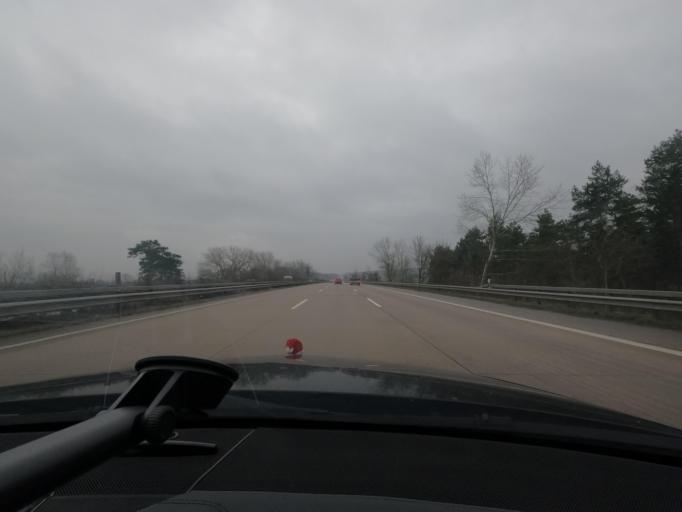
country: DE
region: Lower Saxony
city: Brackel
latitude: 53.3024
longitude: 10.0733
